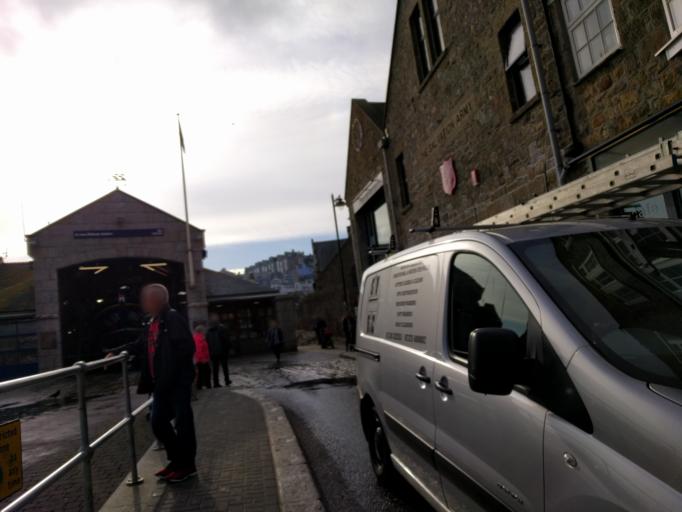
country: GB
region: England
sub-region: Cornwall
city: St Ives
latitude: 50.2131
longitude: -5.4798
